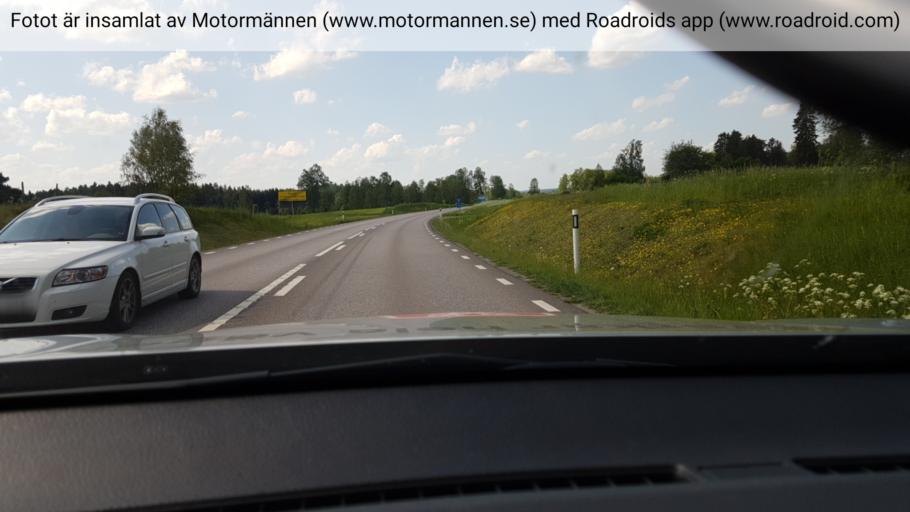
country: SE
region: Vaestra Goetaland
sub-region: Falkopings Kommun
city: Falkoeping
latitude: 58.0123
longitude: 13.5712
